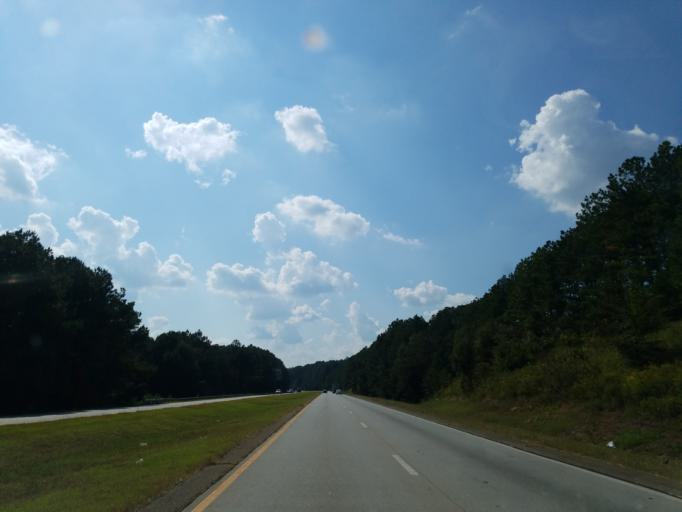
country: US
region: Georgia
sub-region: Oconee County
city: Watkinsville
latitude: 33.9160
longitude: -83.4177
